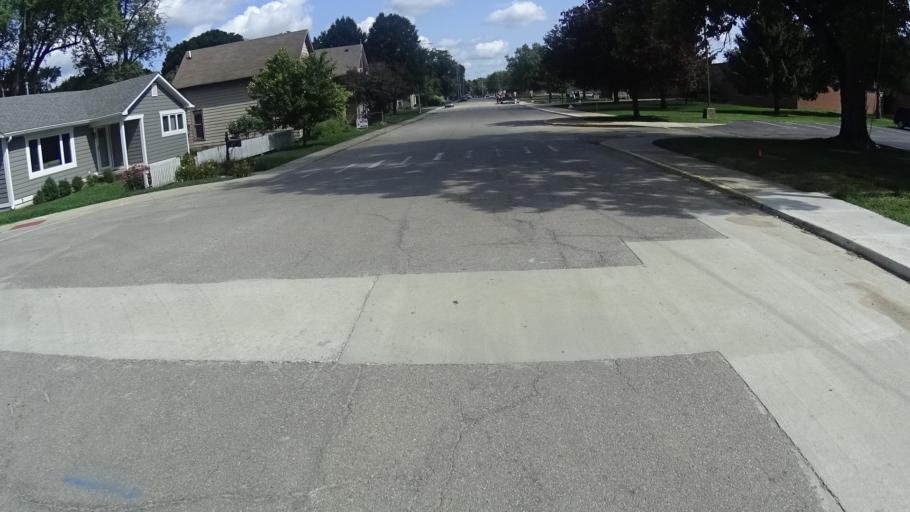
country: US
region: Indiana
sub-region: Madison County
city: Pendleton
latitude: 39.9974
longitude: -85.7415
